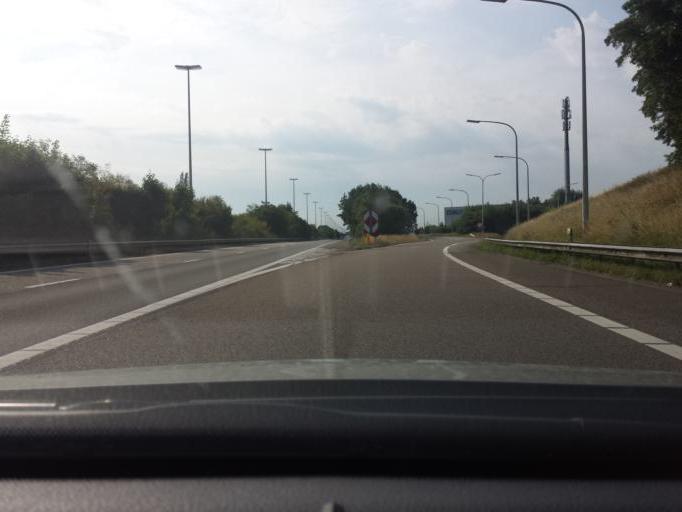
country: BE
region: Flanders
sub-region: Provincie Limburg
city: Tongeren
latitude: 50.7925
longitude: 5.5316
